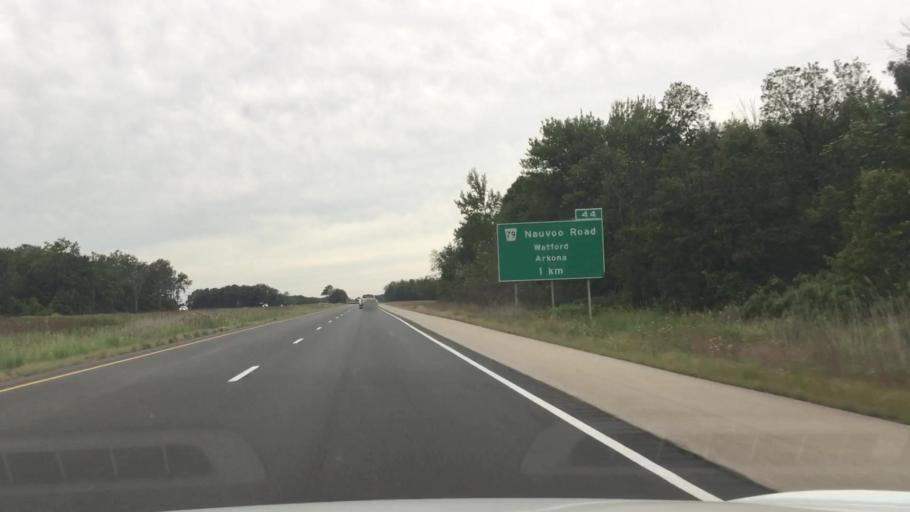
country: CA
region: Ontario
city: Lambton Shores
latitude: 42.9923
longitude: -81.8618
